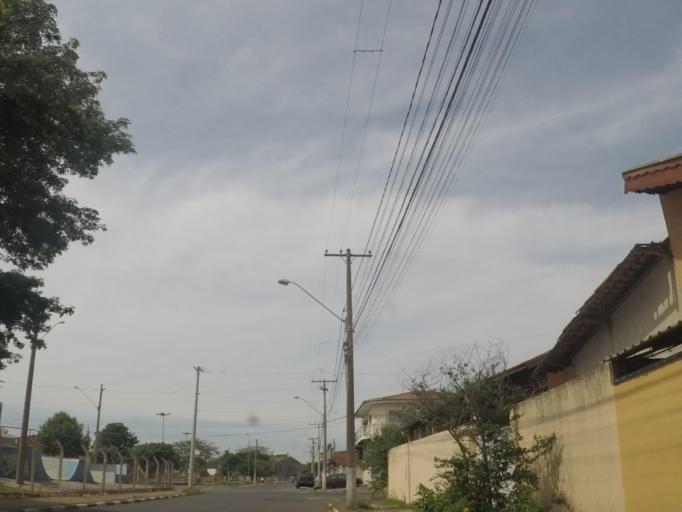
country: BR
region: Sao Paulo
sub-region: Hortolandia
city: Hortolandia
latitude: -22.8570
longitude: -47.1875
